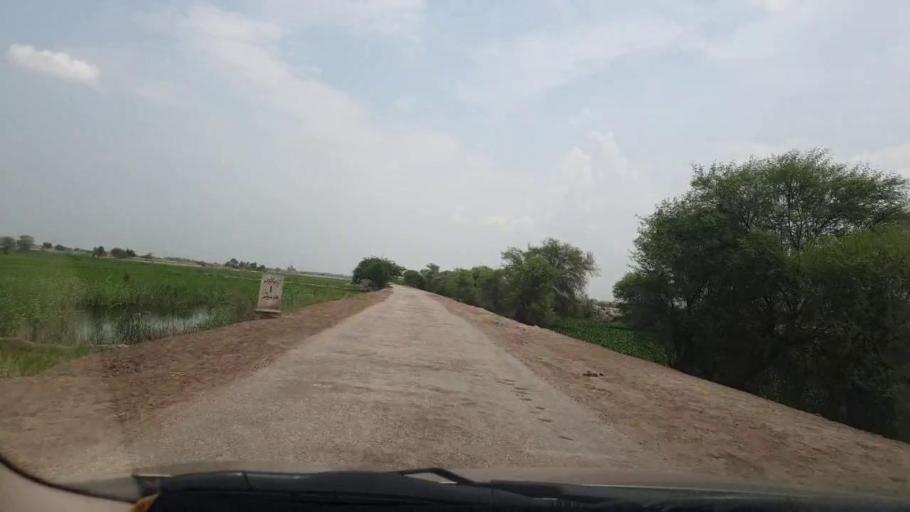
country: PK
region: Sindh
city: Larkana
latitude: 27.6075
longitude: 68.1612
